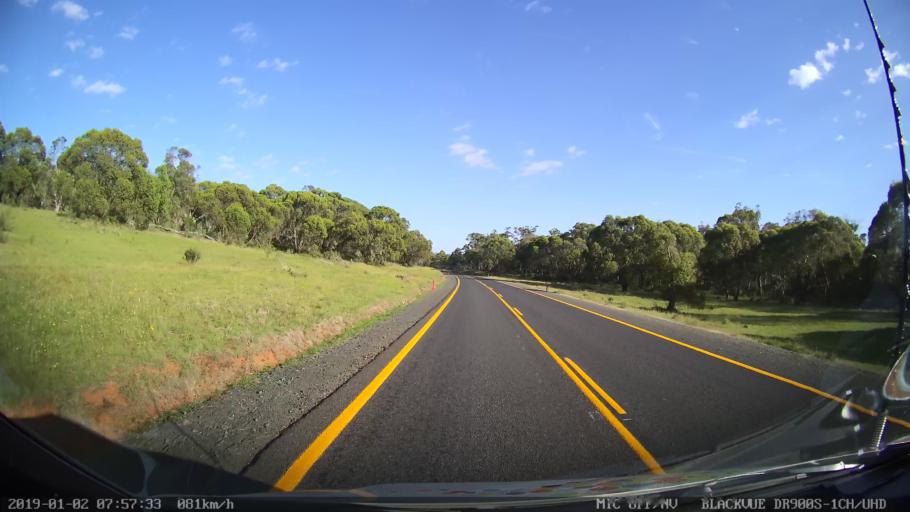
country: AU
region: New South Wales
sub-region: Tumut Shire
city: Tumut
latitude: -35.6624
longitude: 148.4732
